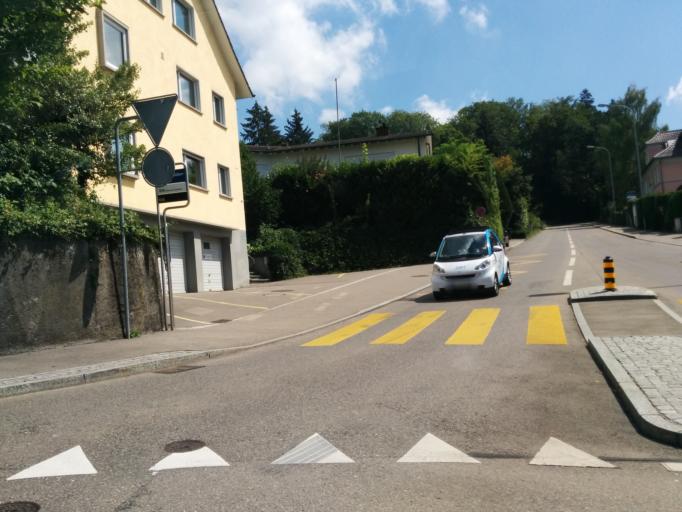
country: CH
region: Zurich
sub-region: Bezirk Meilen
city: Kuesnacht / Goldbach
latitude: 47.3230
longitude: 8.5827
